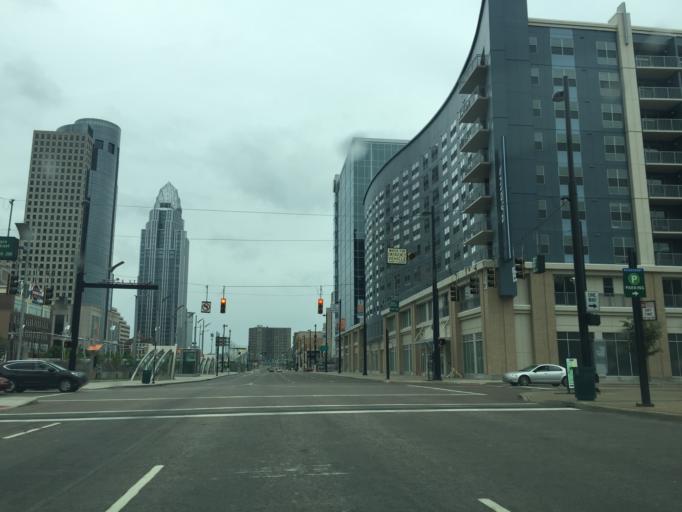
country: US
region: Kentucky
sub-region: Kenton County
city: Covington
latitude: 39.0976
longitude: -84.5142
